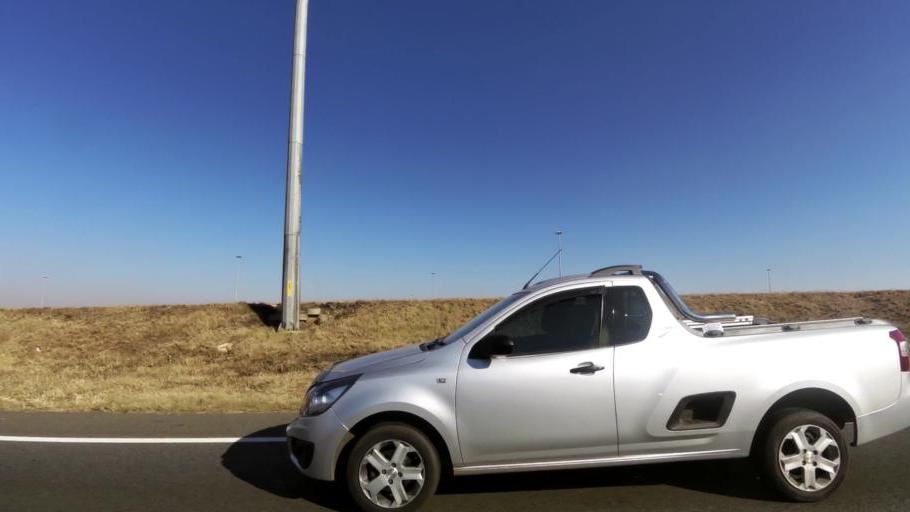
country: ZA
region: Gauteng
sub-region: City of Johannesburg Metropolitan Municipality
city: Johannesburg
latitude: -26.2548
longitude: 27.9648
